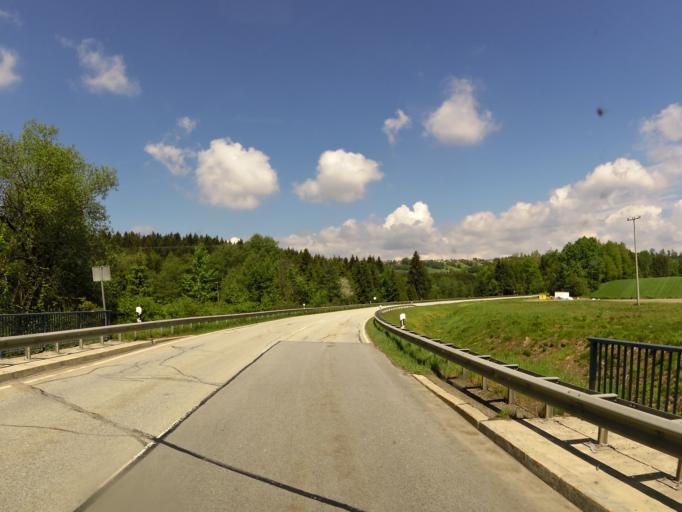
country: DE
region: Bavaria
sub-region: Lower Bavaria
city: Freyung
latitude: 48.8240
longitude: 13.5665
